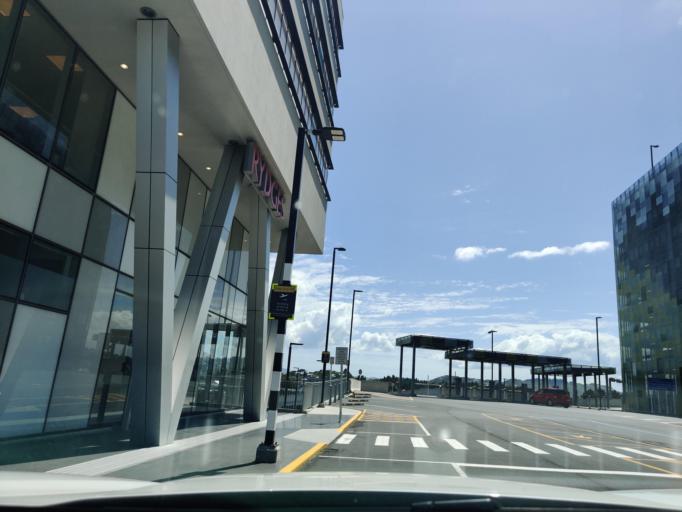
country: NZ
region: Wellington
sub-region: Wellington City
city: Wellington
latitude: -41.3283
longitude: 174.8121
